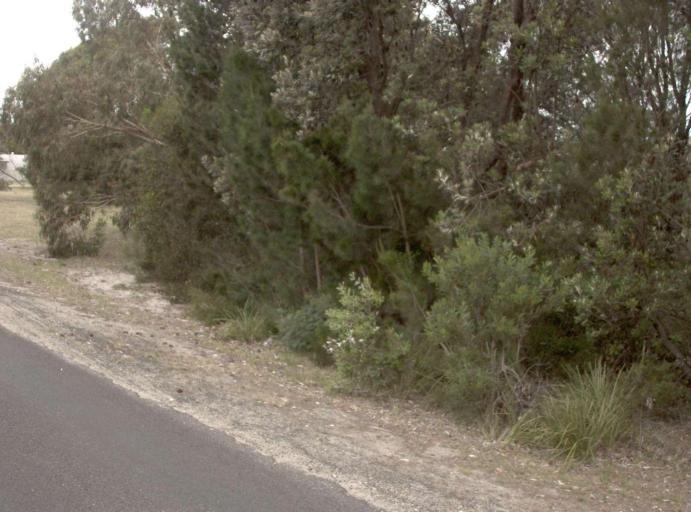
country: AU
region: Victoria
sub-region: East Gippsland
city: Bairnsdale
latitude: -38.0582
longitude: 147.5676
